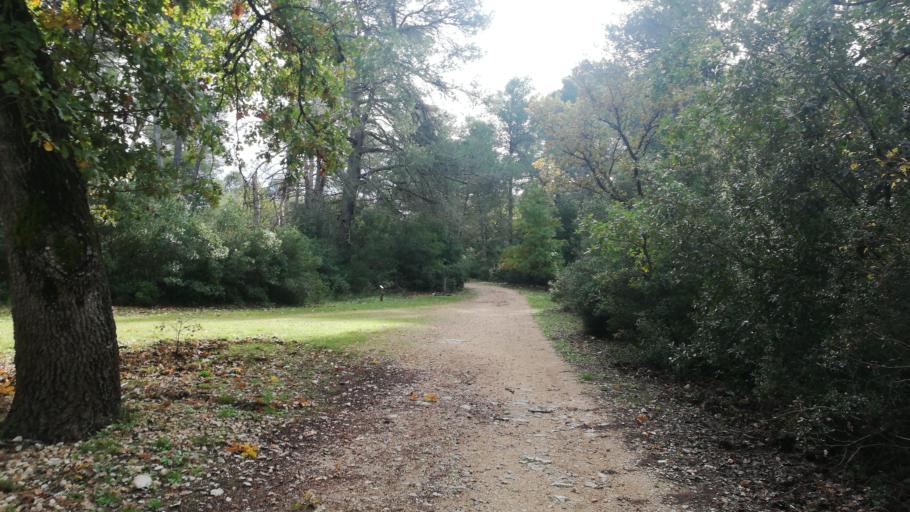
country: IT
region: Apulia
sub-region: Provincia di Bari
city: Cassano delle Murge
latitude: 40.8821
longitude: 16.7092
